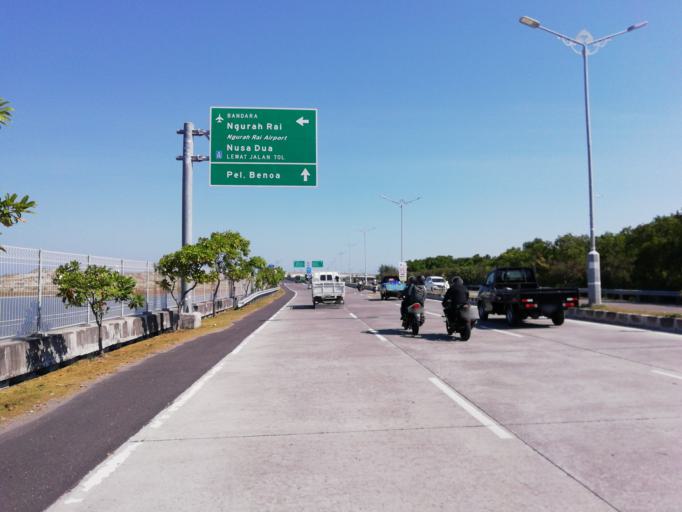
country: ID
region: Bali
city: Karyadharma
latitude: -8.7300
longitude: 115.2128
